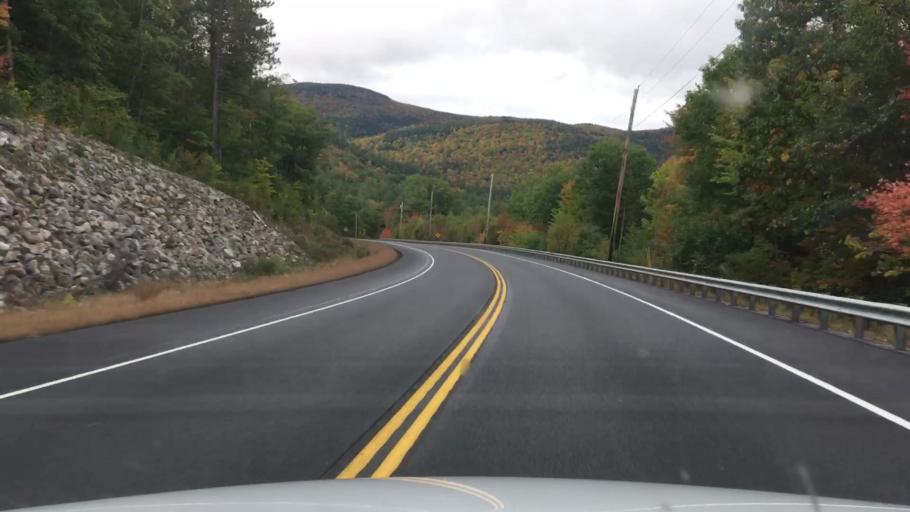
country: US
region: Maine
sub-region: Oxford County
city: Bethel
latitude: 44.4035
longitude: -70.9264
